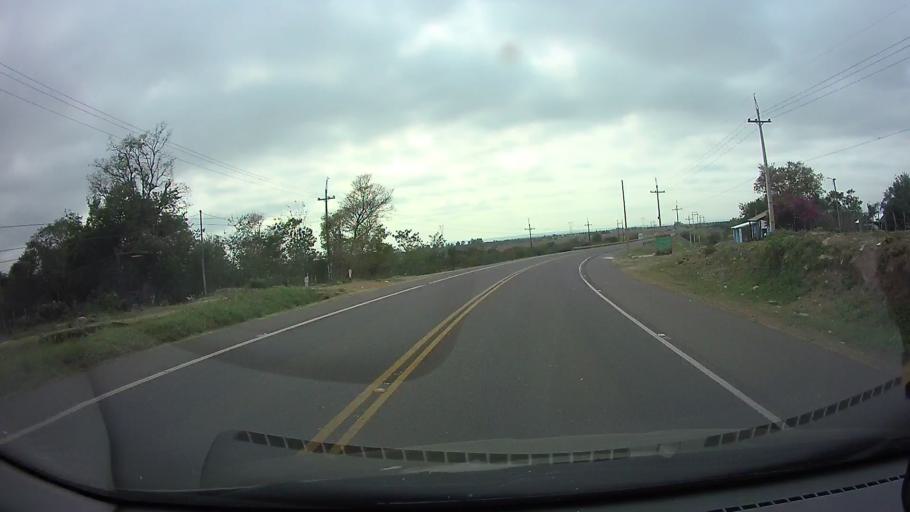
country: PY
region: Cordillera
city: Emboscada
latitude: -25.0884
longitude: -57.2950
